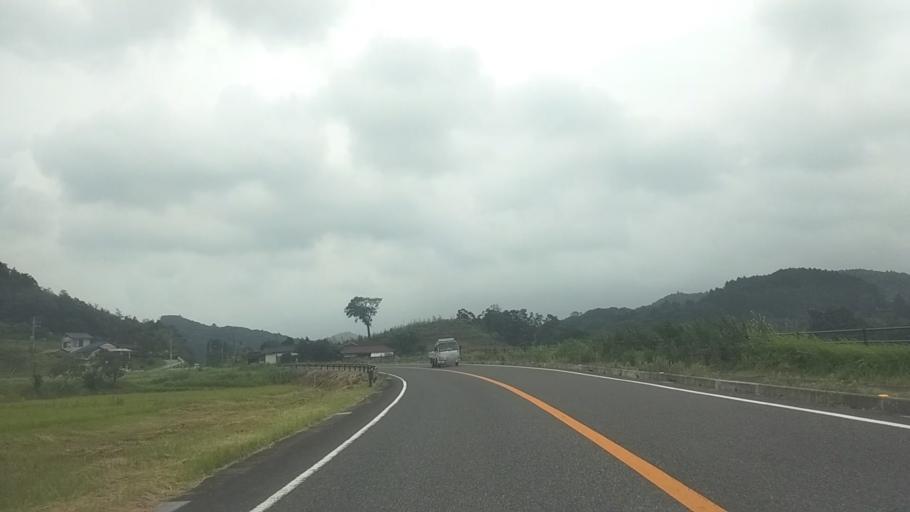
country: JP
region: Chiba
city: Kimitsu
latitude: 35.2191
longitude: 139.9408
